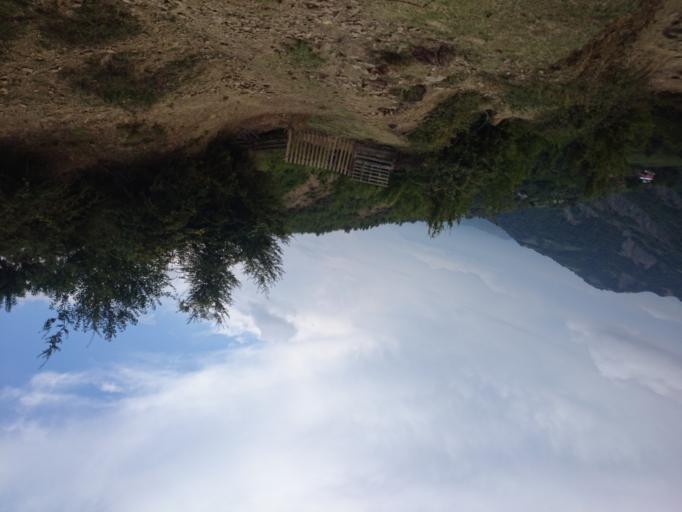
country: AL
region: Elbasan
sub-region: Rrethi i Elbasanit
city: Gjinar
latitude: 40.9871
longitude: 20.2035
